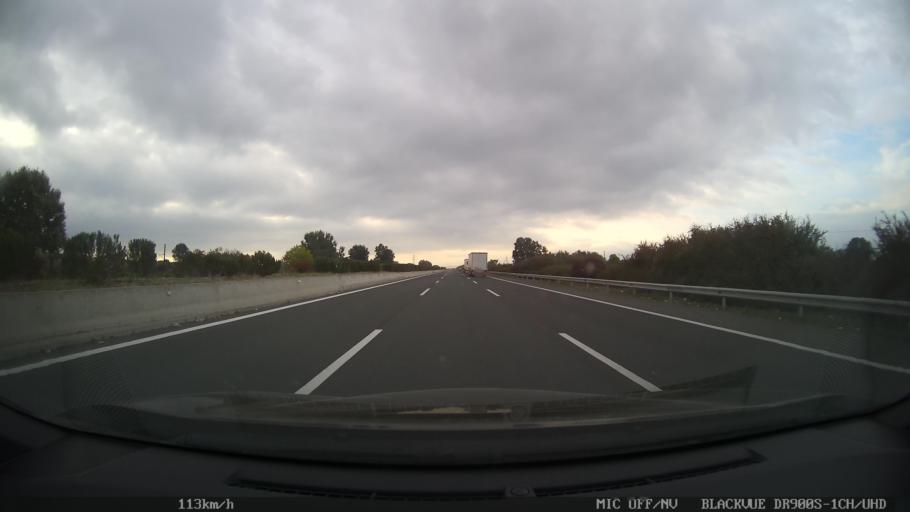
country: GR
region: Central Macedonia
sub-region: Nomos Pierias
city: Nea Efesos
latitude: 40.2229
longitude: 22.5408
